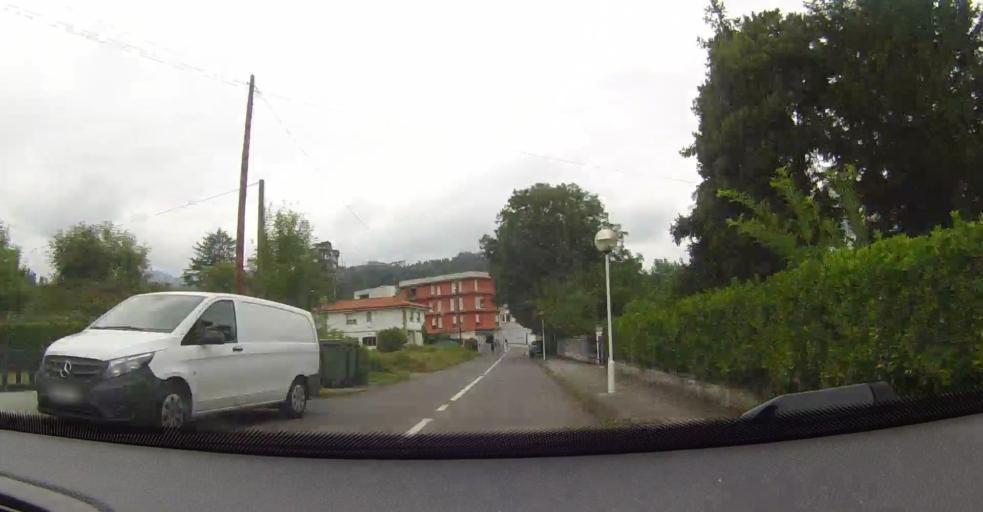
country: ES
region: Basque Country
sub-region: Bizkaia
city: Sopuerta
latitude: 43.2607
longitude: -3.1515
